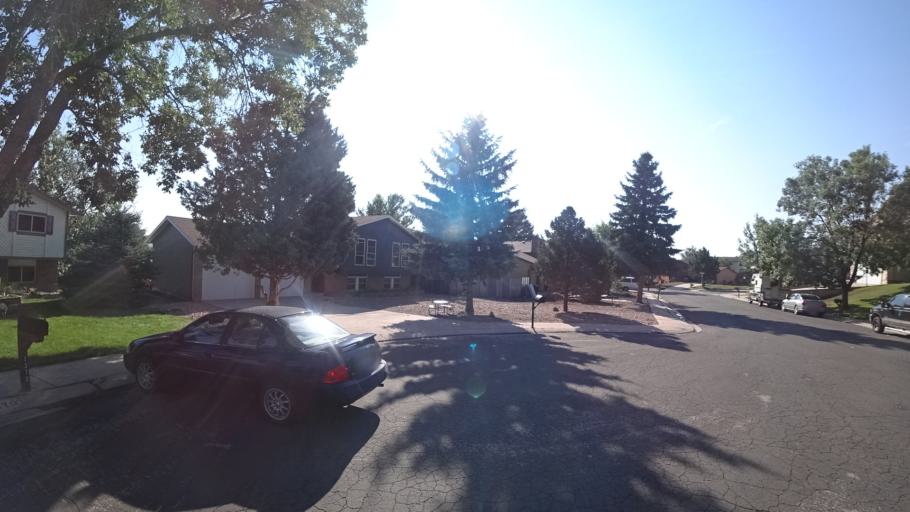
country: US
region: Colorado
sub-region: El Paso County
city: Colorado Springs
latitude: 38.8872
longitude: -104.8488
